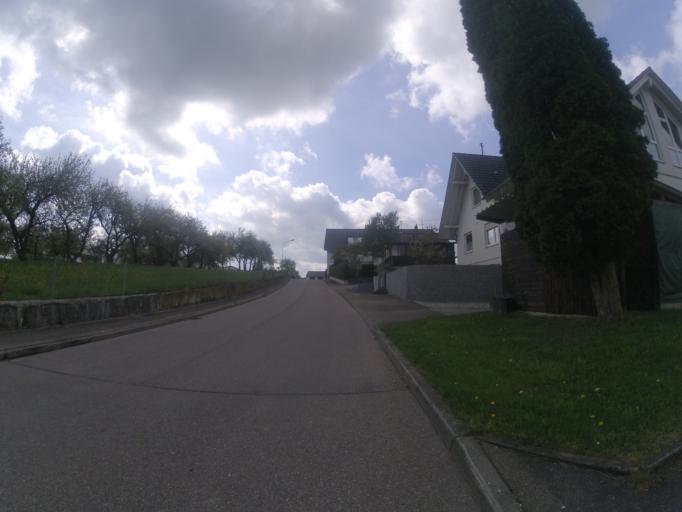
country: DE
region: Baden-Wuerttemberg
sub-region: Tuebingen Region
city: Griesingen
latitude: 48.2330
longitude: 9.7655
